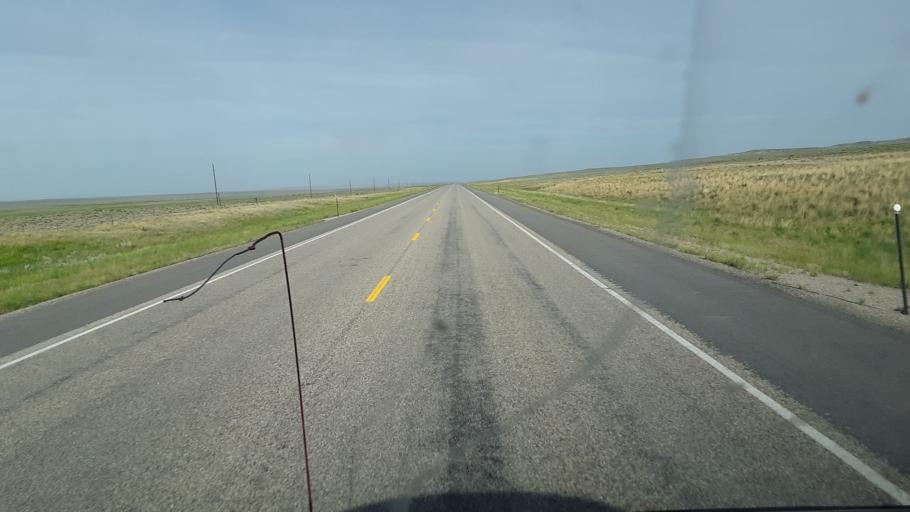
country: US
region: Wyoming
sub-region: Hot Springs County
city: Thermopolis
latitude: 43.1406
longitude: -107.5668
